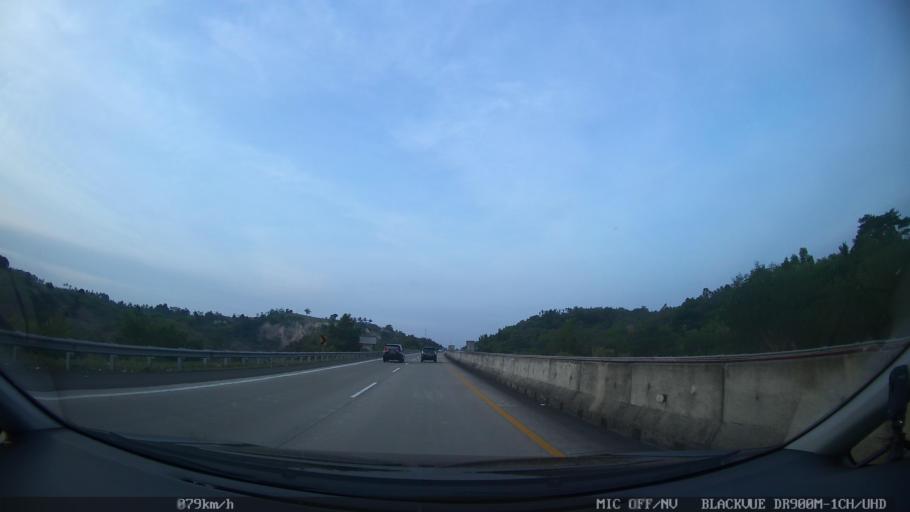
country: ID
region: Lampung
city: Penengahan
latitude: -5.8319
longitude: 105.7320
